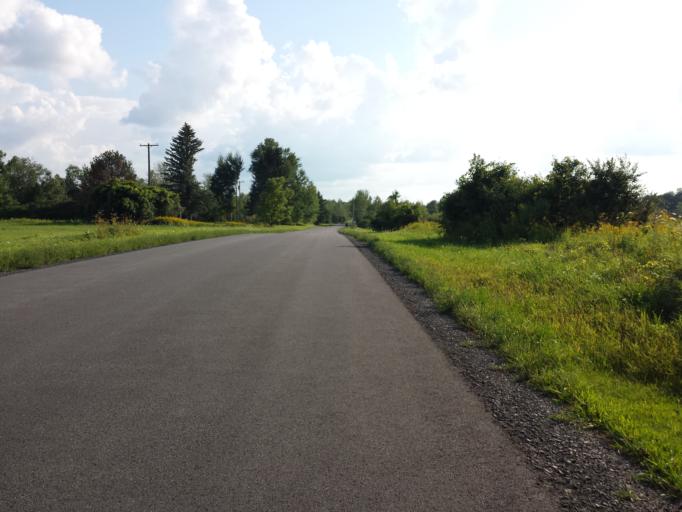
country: US
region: New York
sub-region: St. Lawrence County
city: Potsdam
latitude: 44.6939
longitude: -74.9264
